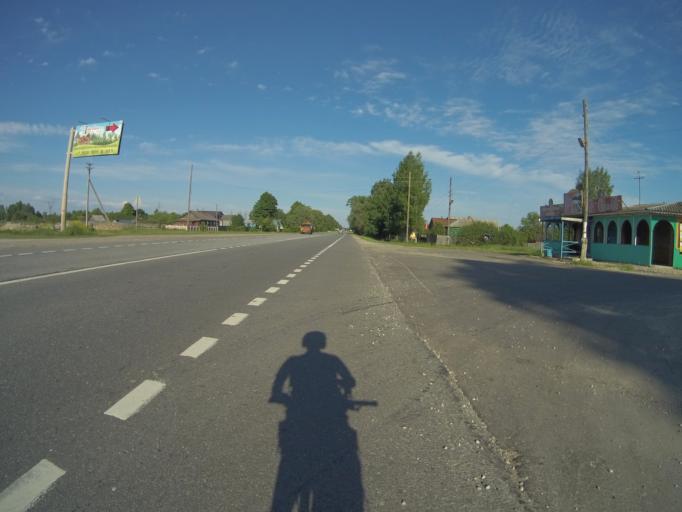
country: RU
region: Vladimir
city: Kameshkovo
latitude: 56.1984
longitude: 40.8430
